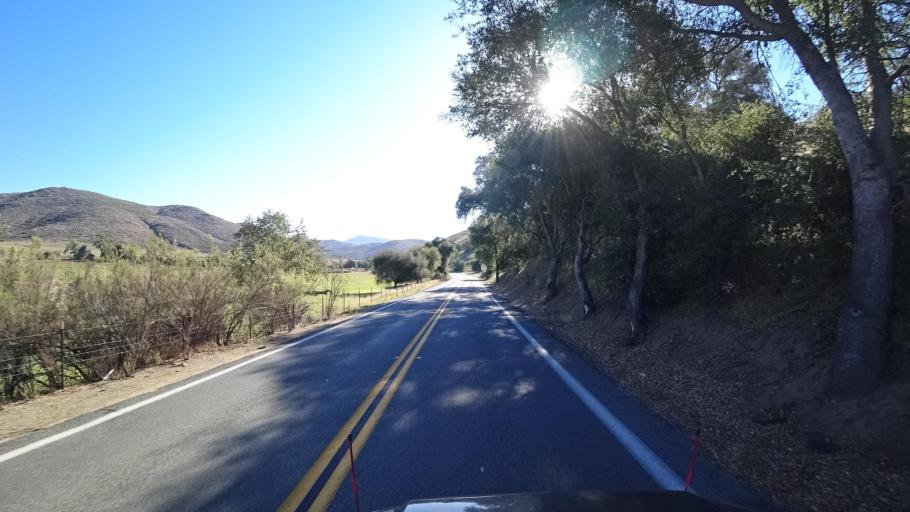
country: US
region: California
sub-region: San Diego County
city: Jamul
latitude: 32.6681
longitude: -116.8276
